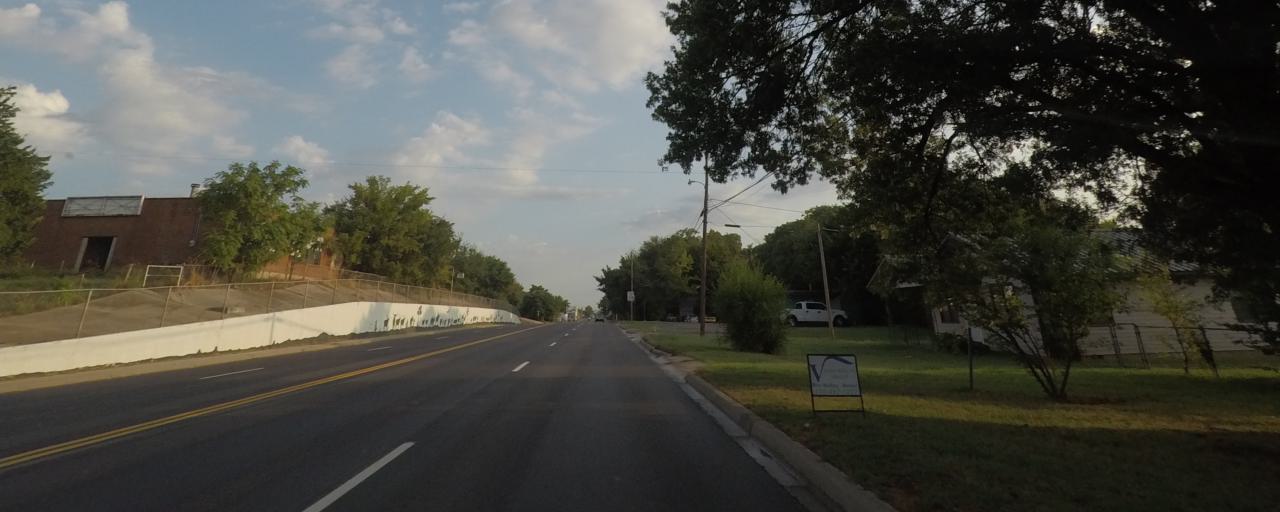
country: US
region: Oklahoma
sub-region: Stephens County
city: Comanche
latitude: 34.3638
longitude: -97.9642
